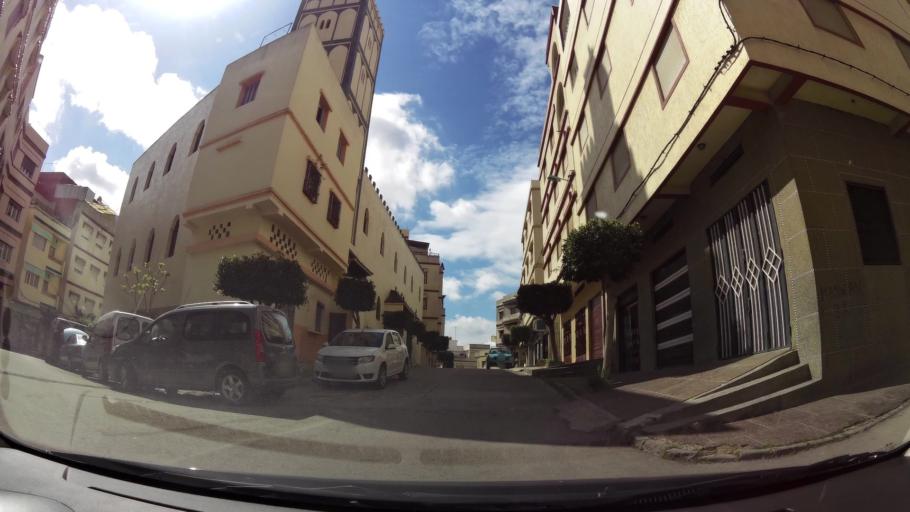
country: MA
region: Tanger-Tetouan
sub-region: Tanger-Assilah
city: Tangier
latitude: 35.7748
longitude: -5.8272
